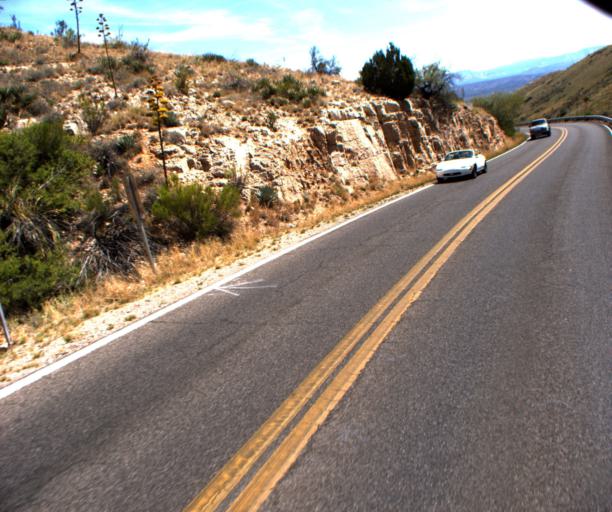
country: US
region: Arizona
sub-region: Yavapai County
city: Clarkdale
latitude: 34.7499
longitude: -112.1007
